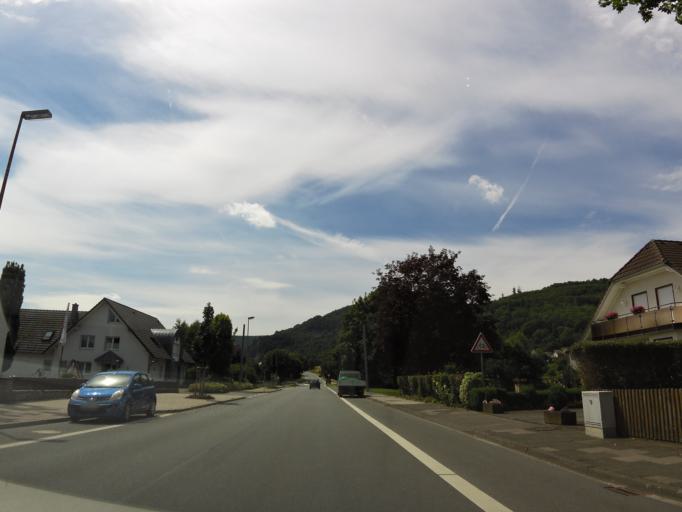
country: DE
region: North Rhine-Westphalia
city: Beverungen
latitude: 51.6583
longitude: 9.3716
